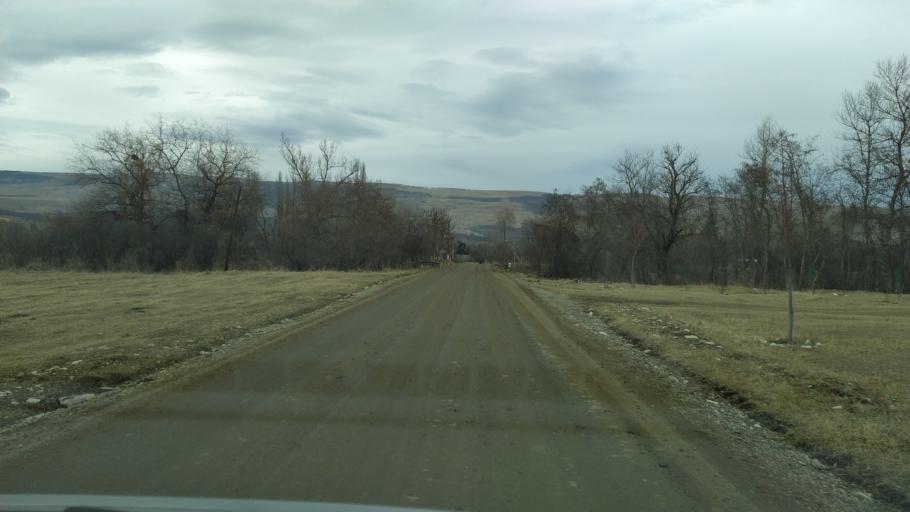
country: RU
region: Krasnodarskiy
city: Peredovaya
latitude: 44.0852
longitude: 41.3645
